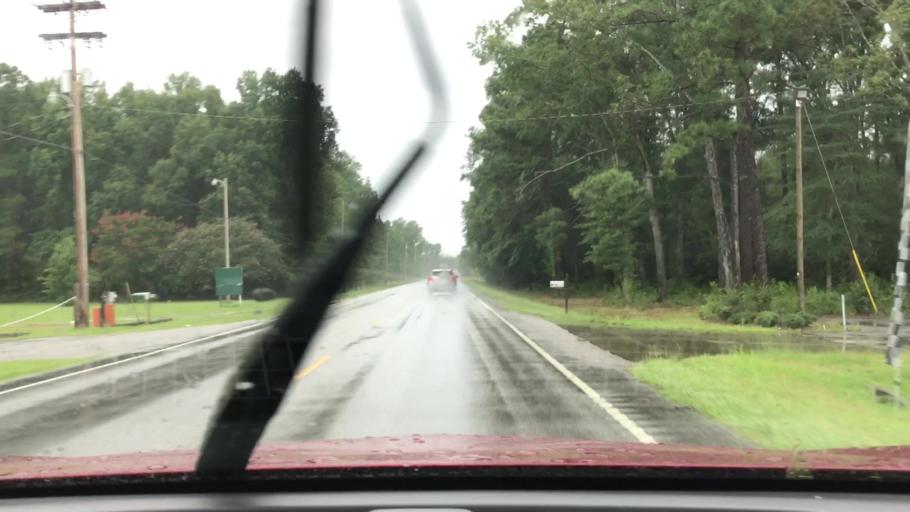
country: US
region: South Carolina
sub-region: Horry County
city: Conway
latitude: 33.7869
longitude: -79.0755
